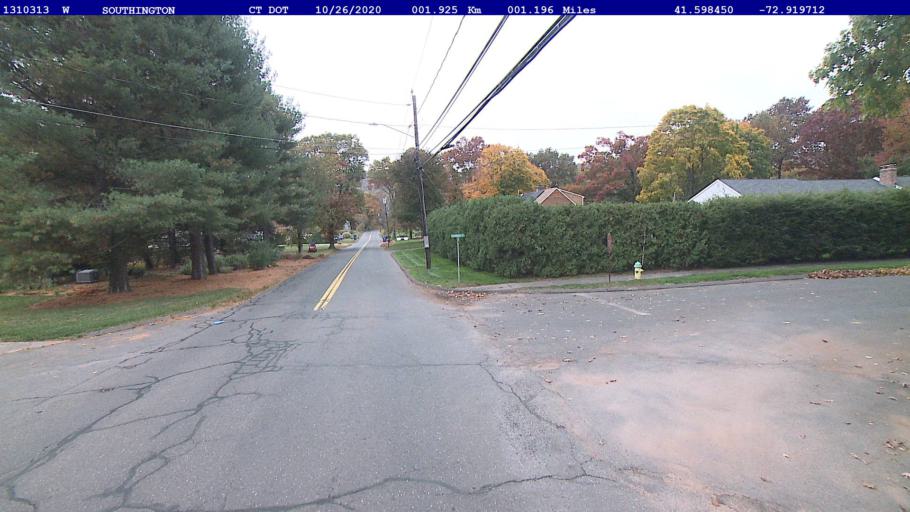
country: US
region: Connecticut
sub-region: New Haven County
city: Wolcott
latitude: 41.5984
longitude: -72.9197
